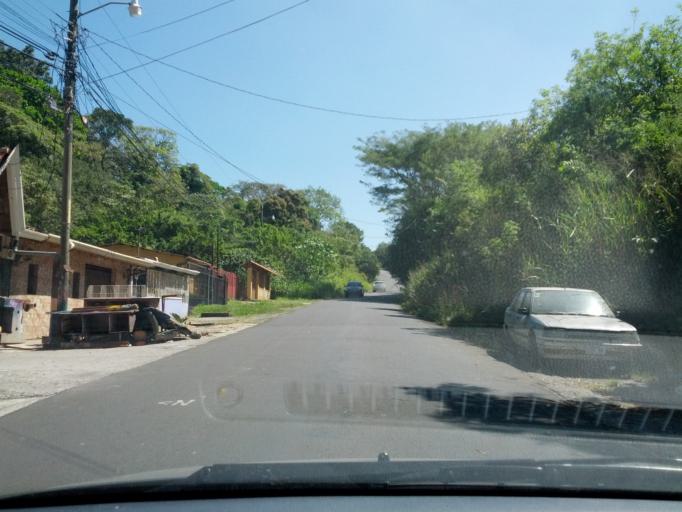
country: CR
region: Alajuela
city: Alajuela
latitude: 10.0089
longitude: -84.1997
